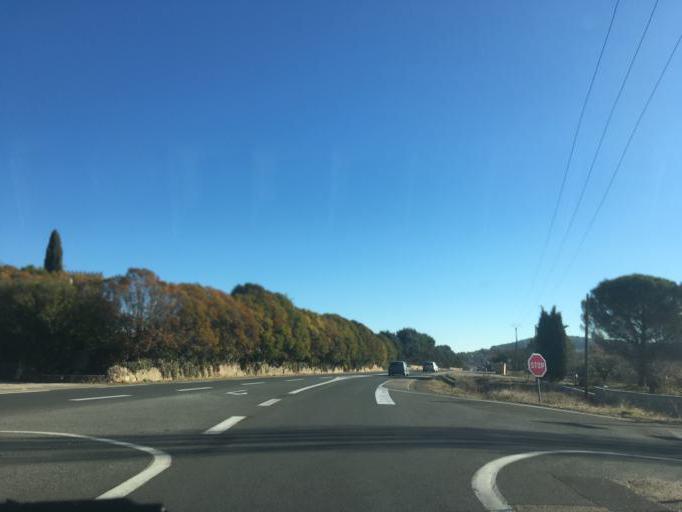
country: FR
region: Provence-Alpes-Cote d'Azur
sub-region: Departement du Var
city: Flayosc
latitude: 43.5288
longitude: 6.4272
